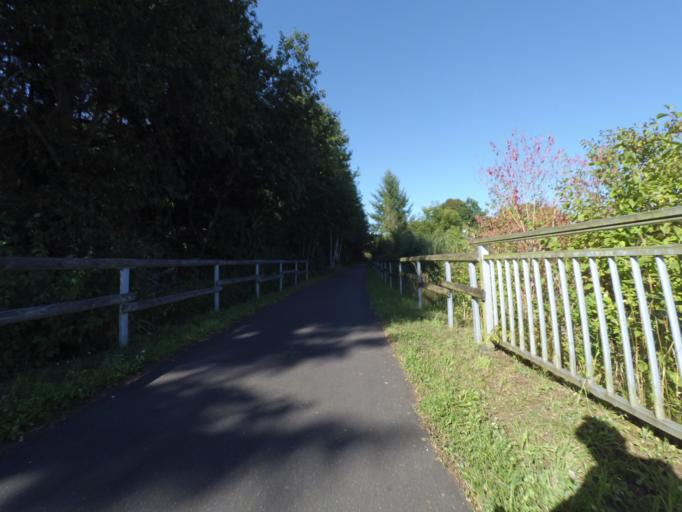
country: DE
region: Rheinland-Pfalz
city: Schalkenmehren
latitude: 50.1676
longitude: 6.8683
